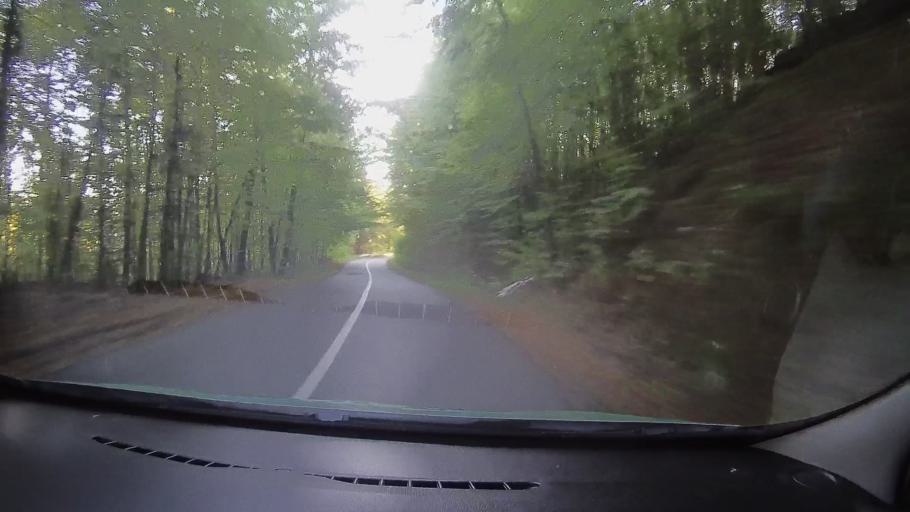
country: RO
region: Timis
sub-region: Comuna Nadrag
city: Nadrag
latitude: 45.6756
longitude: 22.1655
